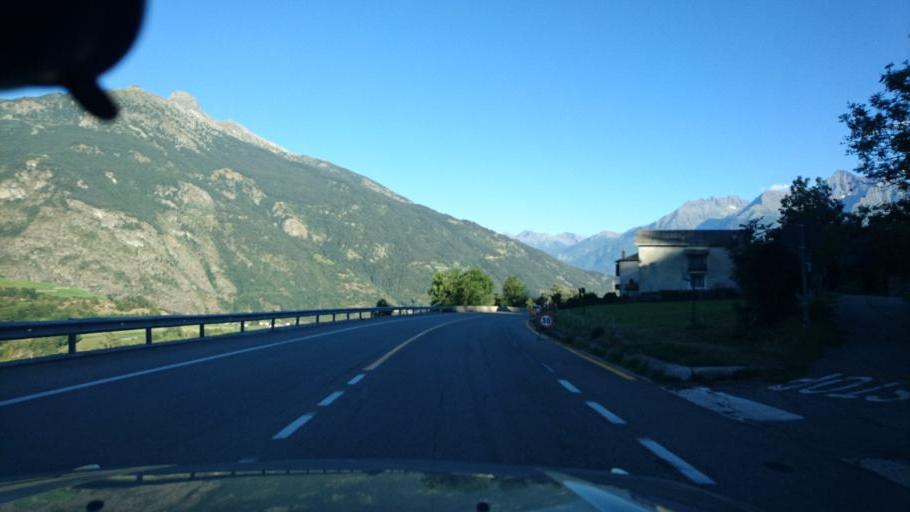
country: IT
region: Aosta Valley
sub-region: Valle d'Aosta
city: Allein
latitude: 45.7962
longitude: 7.2826
